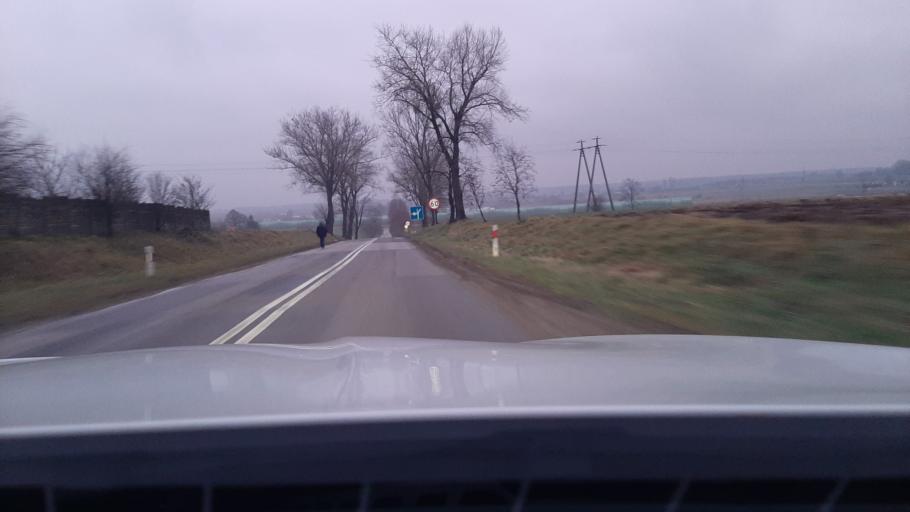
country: PL
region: Lublin Voivodeship
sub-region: Powiat lubelski
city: Garbow
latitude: 51.3463
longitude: 22.3647
